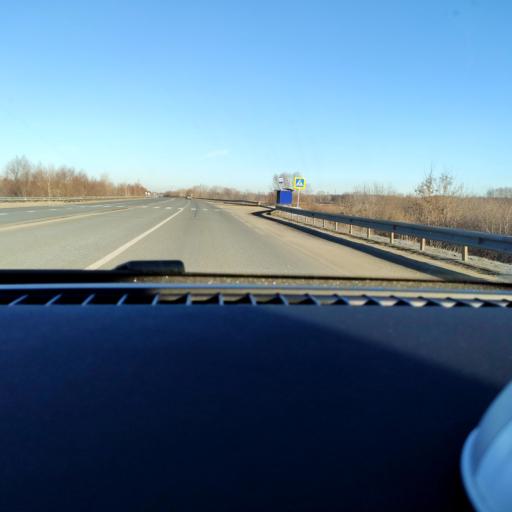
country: RU
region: Samara
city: Novokuybyshevsk
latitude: 53.1292
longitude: 49.9543
